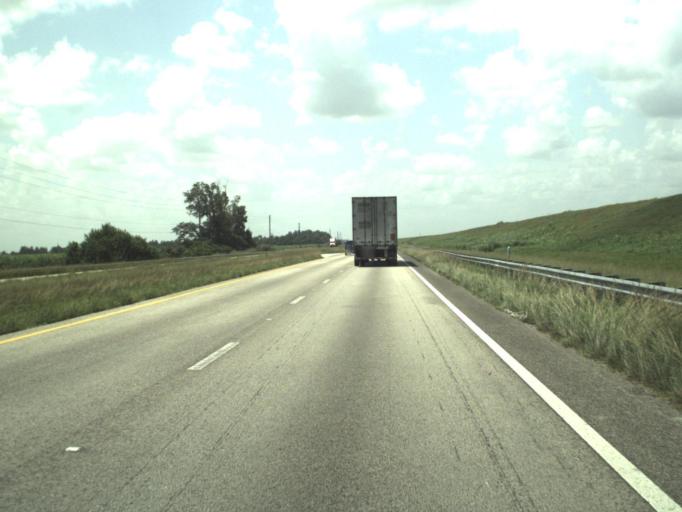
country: US
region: Florida
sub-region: Hendry County
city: Clewiston
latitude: 26.7347
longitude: -80.8668
